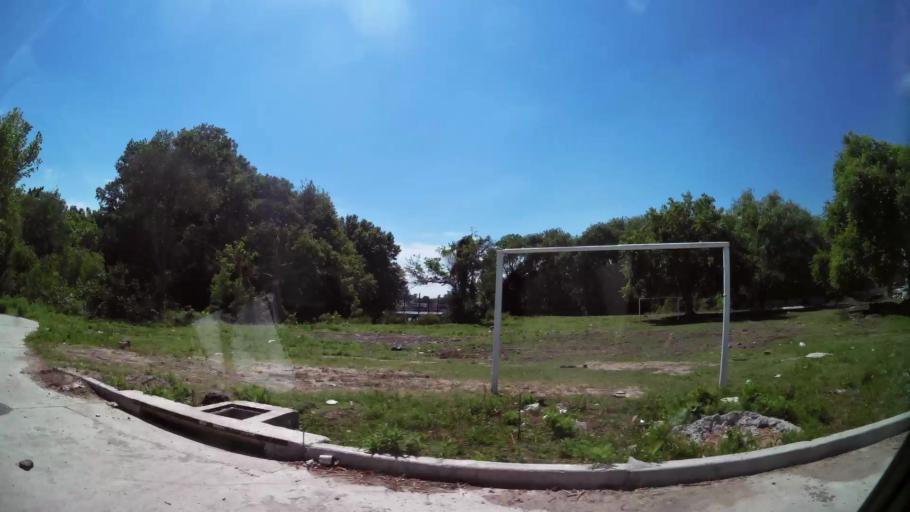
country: AR
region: Buenos Aires
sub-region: Partido de Tigre
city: Tigre
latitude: -34.4250
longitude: -58.5609
